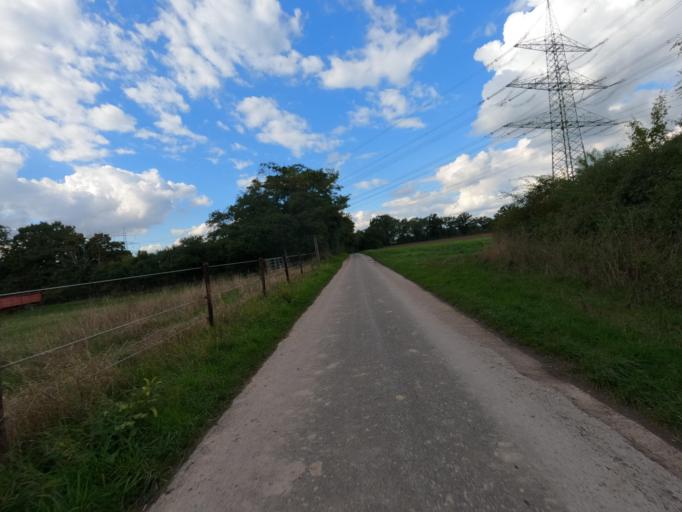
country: DE
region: North Rhine-Westphalia
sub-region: Regierungsbezirk Koln
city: Aldenhoven
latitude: 50.9364
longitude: 6.3025
